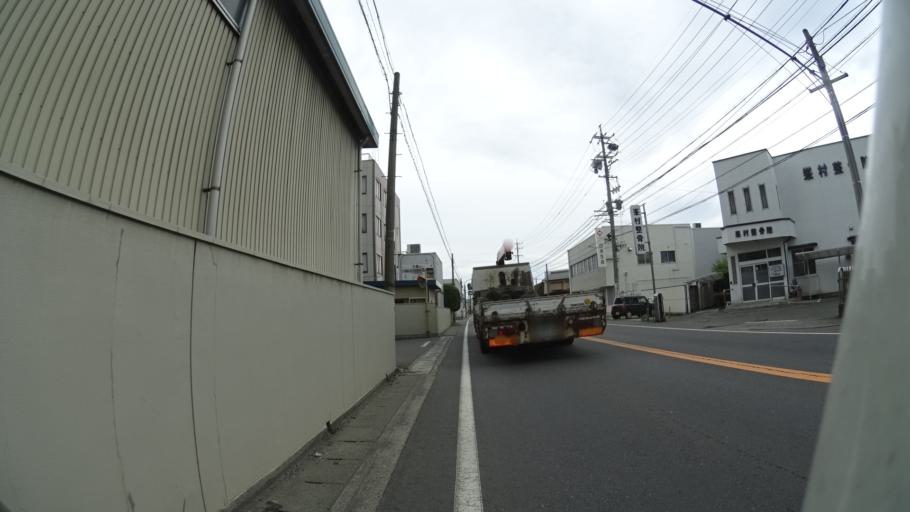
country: JP
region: Nagano
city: Nagano-shi
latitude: 36.5753
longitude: 138.1439
